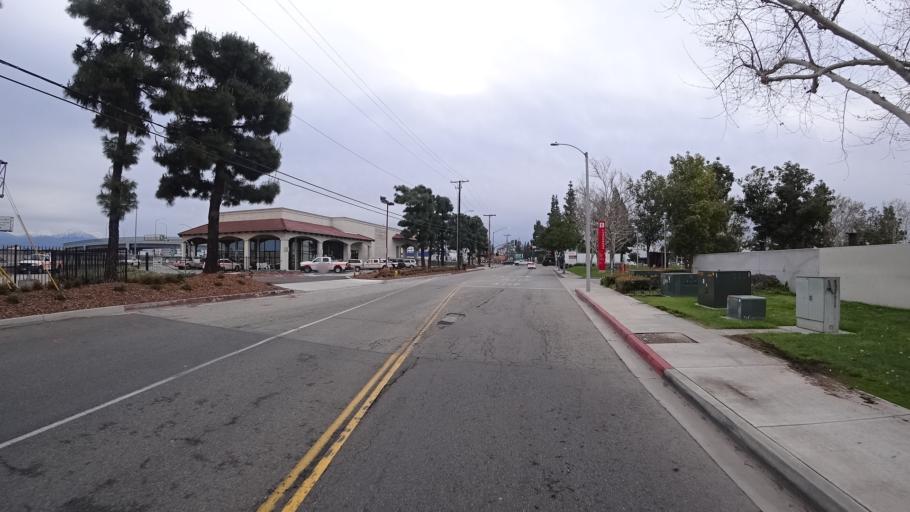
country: US
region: California
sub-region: Los Angeles County
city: West Puente Valley
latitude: 34.0668
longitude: -117.9841
